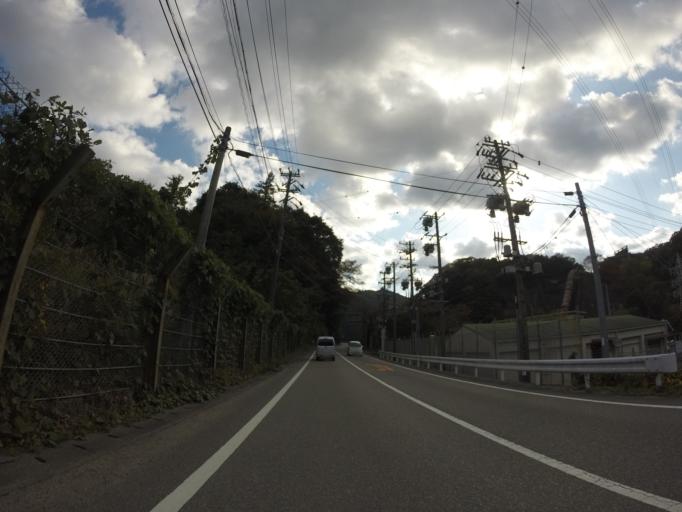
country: JP
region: Shizuoka
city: Kanaya
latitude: 34.9016
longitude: 138.1123
